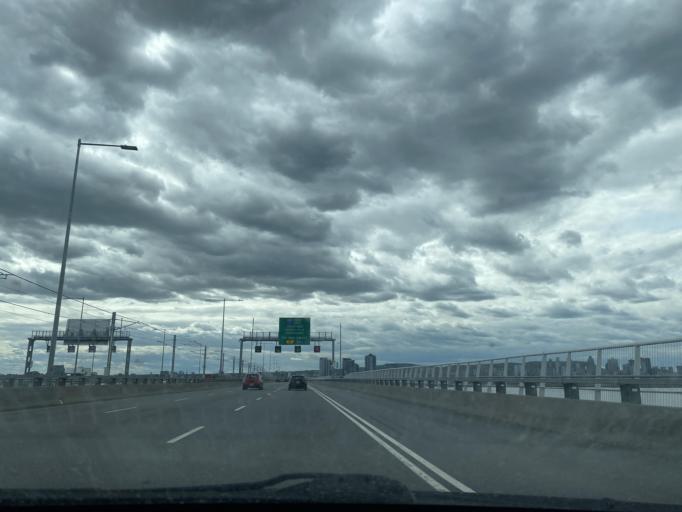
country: CA
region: Quebec
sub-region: Monteregie
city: Brossard
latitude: 45.4692
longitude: -73.5119
